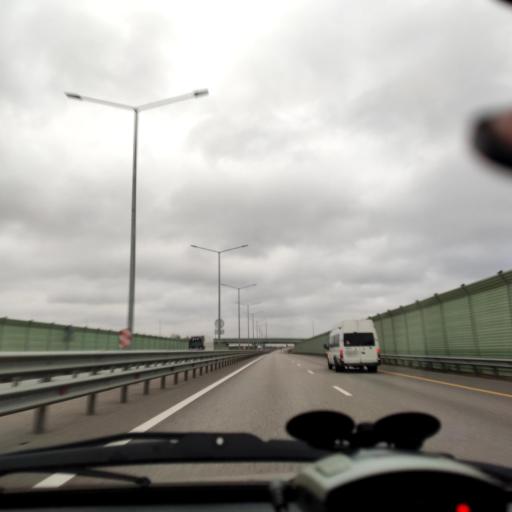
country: RU
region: Voronezj
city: Novaya Usman'
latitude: 51.6036
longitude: 39.3343
